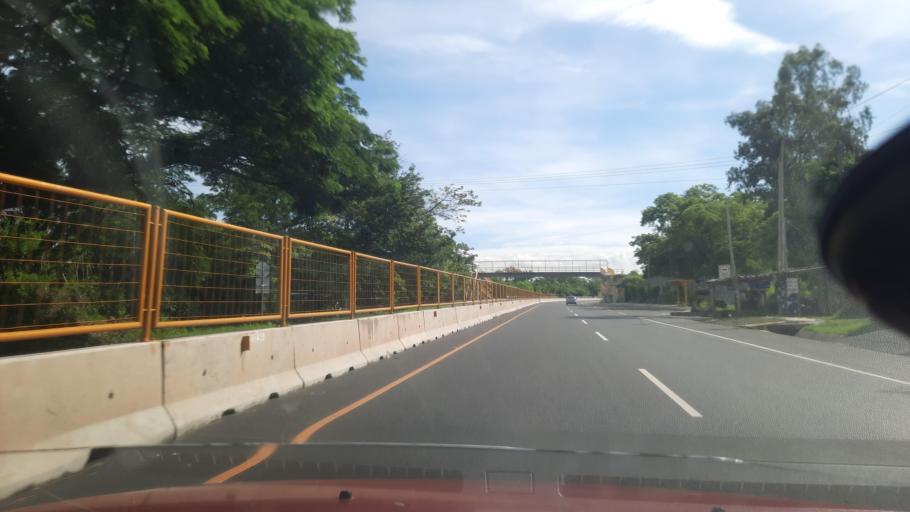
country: SV
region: La Paz
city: El Rosario
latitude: 13.4807
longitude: -88.9988
